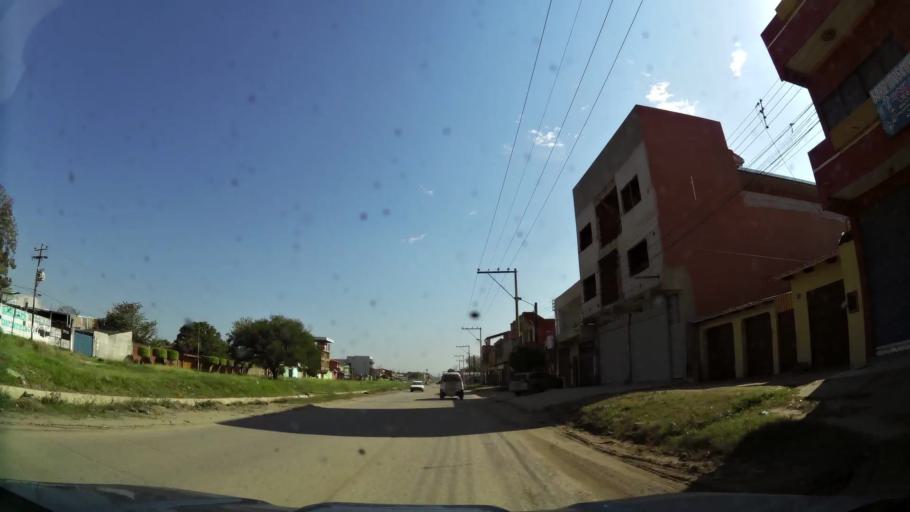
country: BO
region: Santa Cruz
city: Santa Cruz de la Sierra
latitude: -17.8206
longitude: -63.1235
